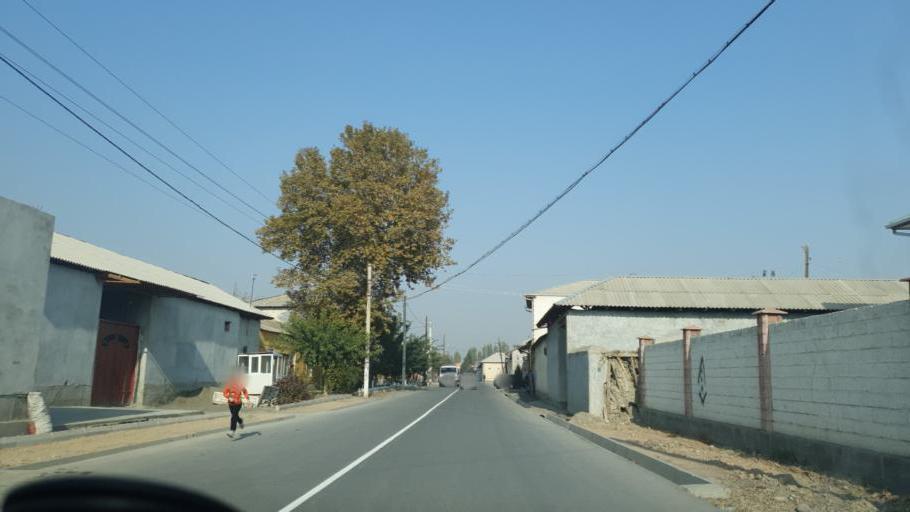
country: UZ
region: Fergana
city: Qo`qon
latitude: 40.5797
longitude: 70.9135
